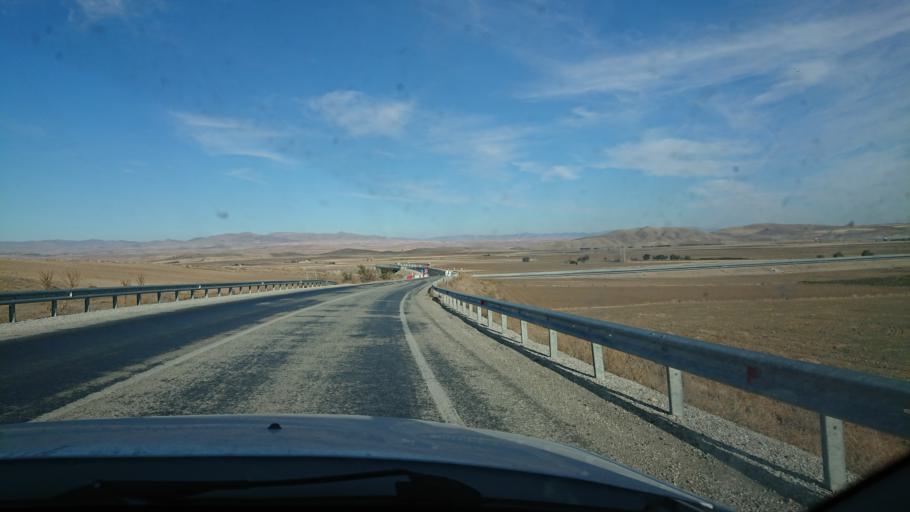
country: TR
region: Aksaray
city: Sariyahsi
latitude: 38.9969
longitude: 33.8510
